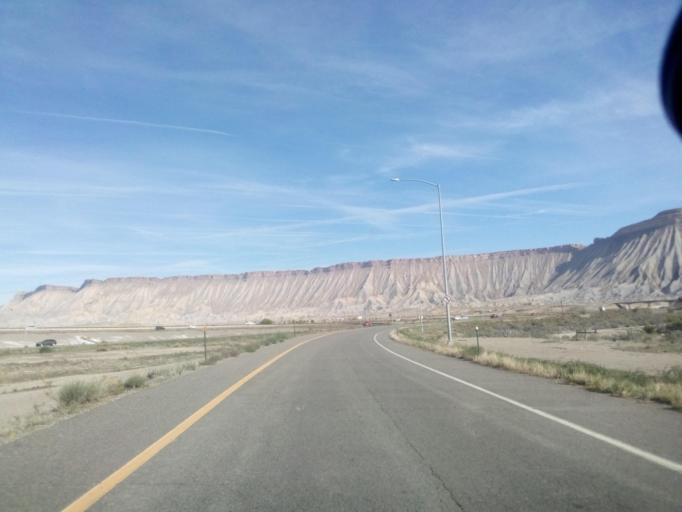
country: US
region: Colorado
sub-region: Mesa County
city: Clifton
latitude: 39.1032
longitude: -108.4467
